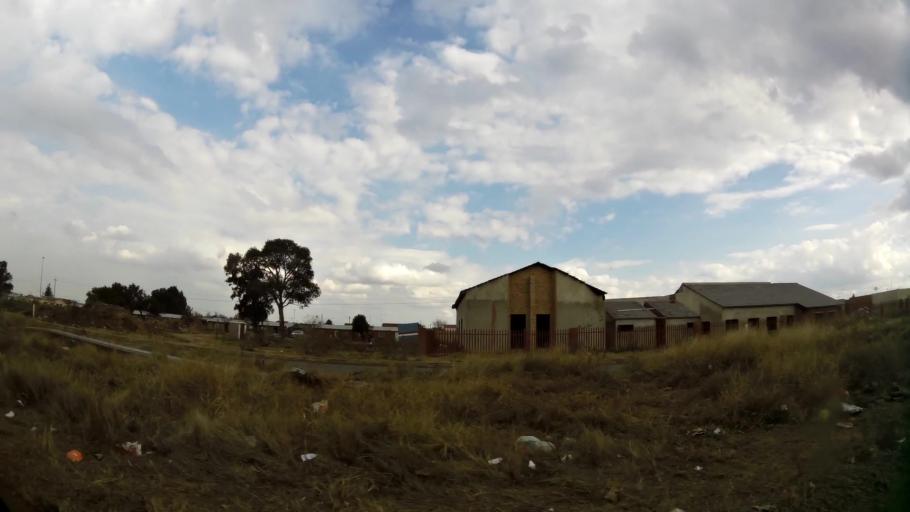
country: ZA
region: Gauteng
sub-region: Sedibeng District Municipality
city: Vanderbijlpark
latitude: -26.6616
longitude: 27.8504
